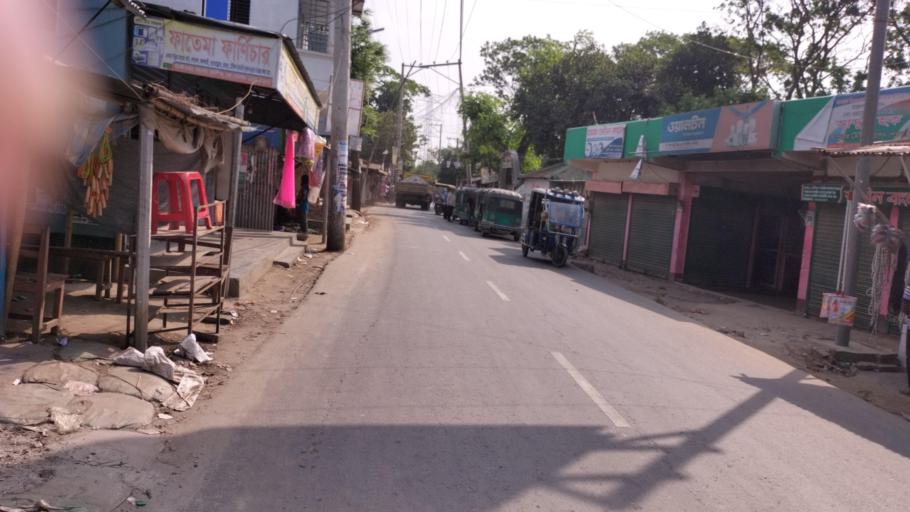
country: BD
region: Dhaka
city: Azimpur
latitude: 23.7554
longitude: 90.2924
